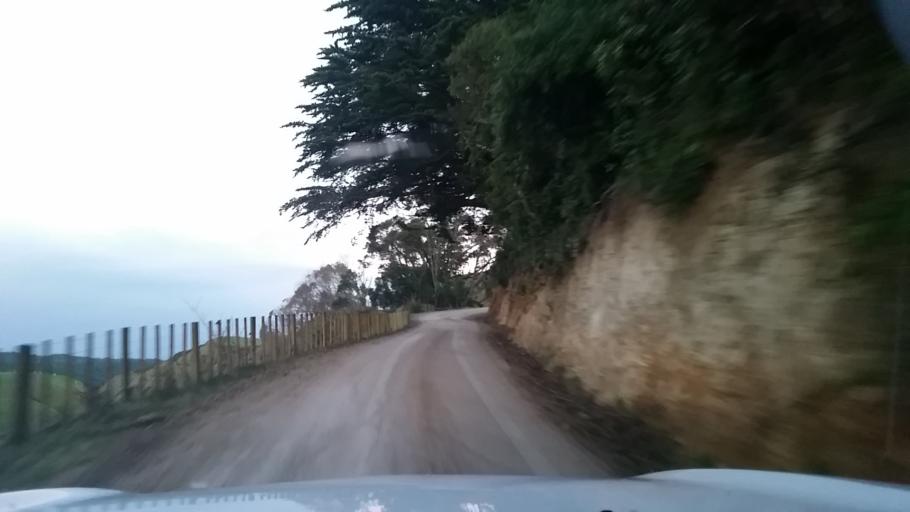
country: NZ
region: Manawatu-Wanganui
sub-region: Wanganui District
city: Wanganui
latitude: -39.7673
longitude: 174.8716
